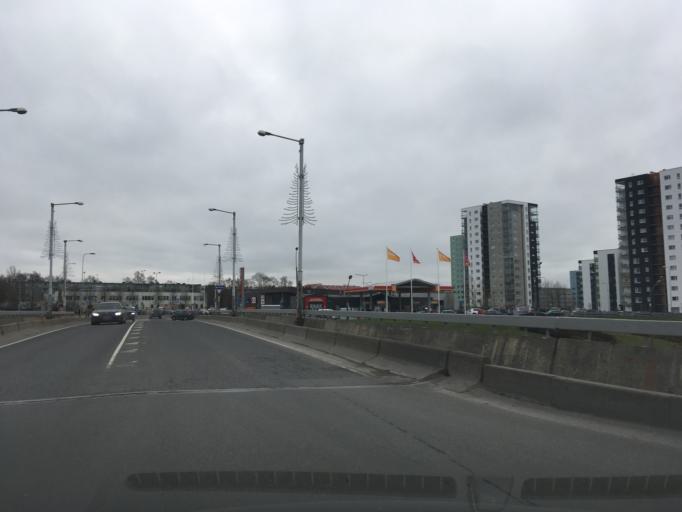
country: EE
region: Harju
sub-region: Tallinna linn
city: Tallinn
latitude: 59.4369
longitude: 24.8104
